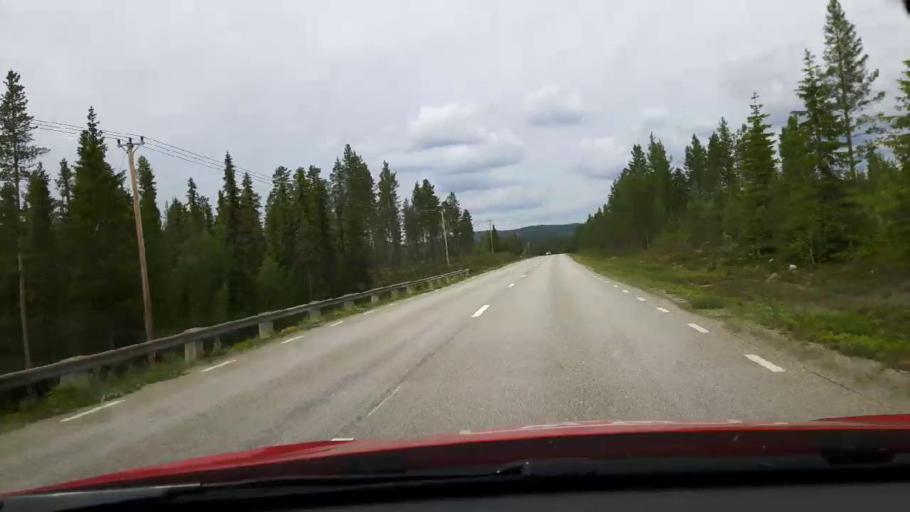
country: SE
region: Jaemtland
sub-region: Harjedalens Kommun
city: Sveg
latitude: 62.3996
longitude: 13.7443
